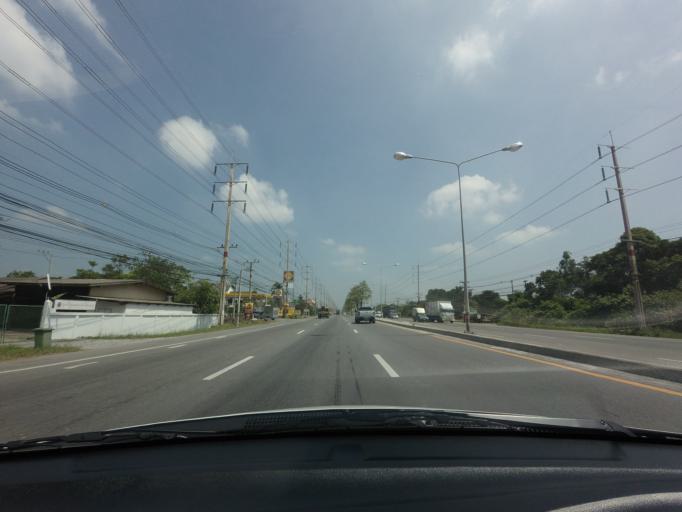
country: TH
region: Chachoengsao
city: Bang Pakong
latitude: 13.5797
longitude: 101.0067
